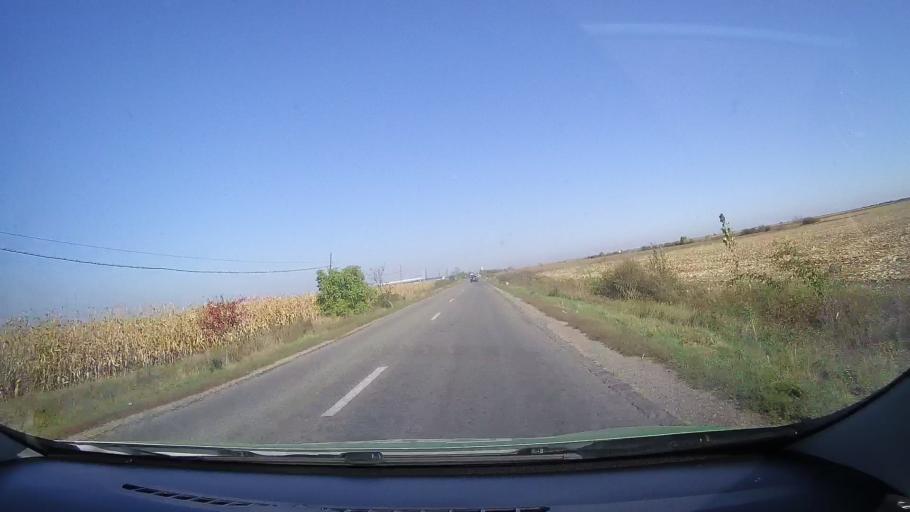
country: RO
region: Satu Mare
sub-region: Oras Tasnad
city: Tasnad
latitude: 47.4992
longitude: 22.5748
